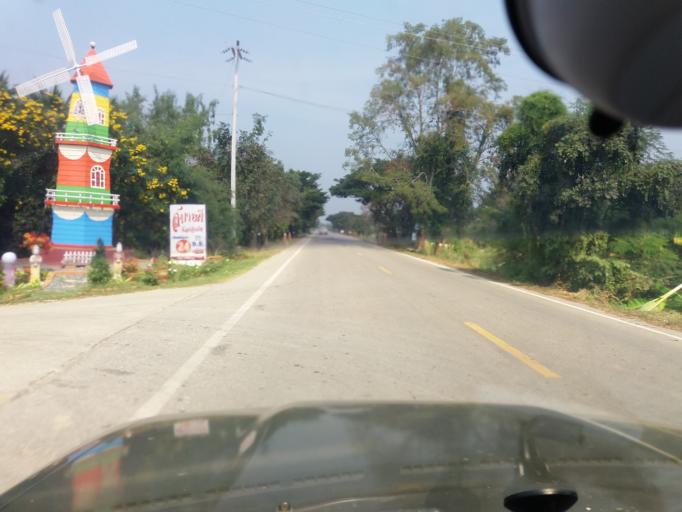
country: TH
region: Sing Buri
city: Bang Racham
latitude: 14.8927
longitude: 100.2709
